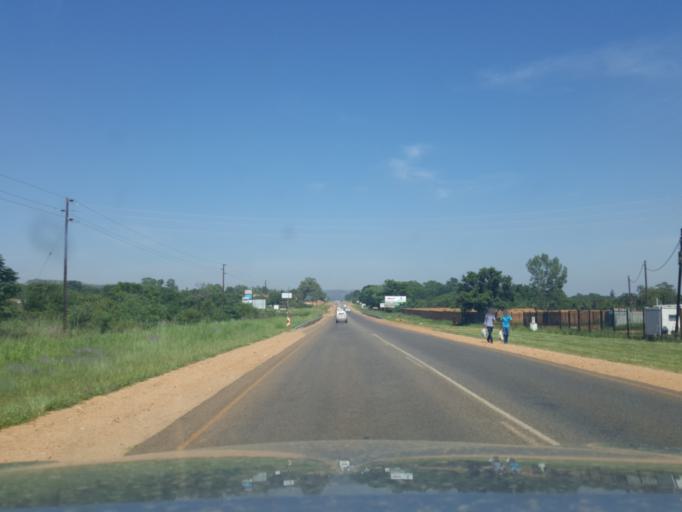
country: ZA
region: Gauteng
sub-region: City of Tshwane Metropolitan Municipality
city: Pretoria
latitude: -25.6783
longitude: 28.3234
